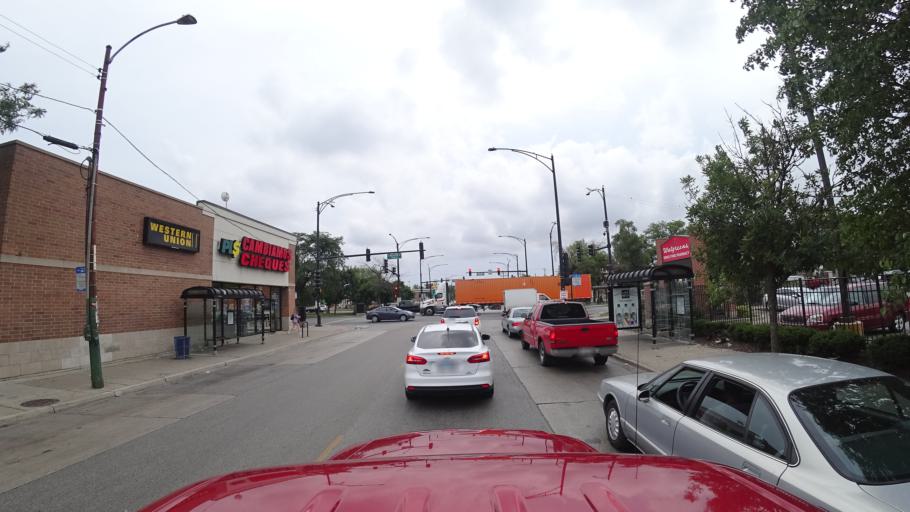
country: US
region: Illinois
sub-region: Cook County
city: Chicago
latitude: 41.8084
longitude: -87.6850
